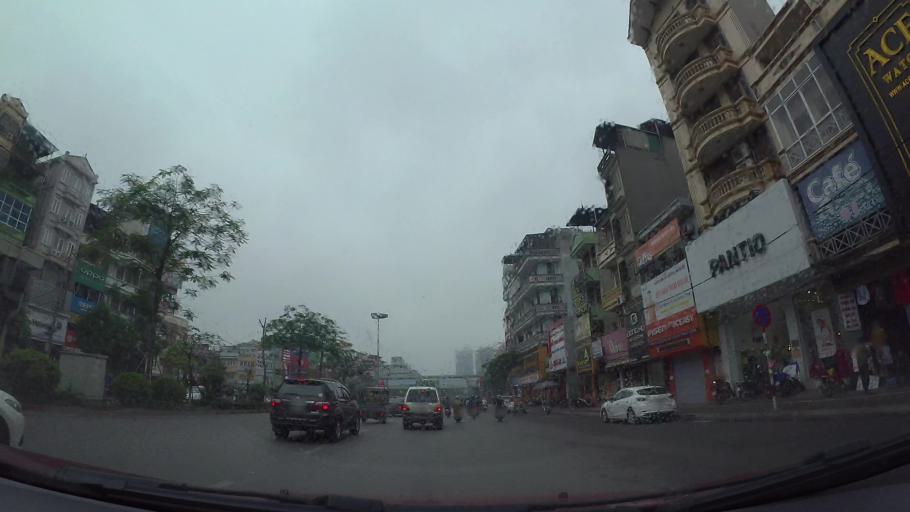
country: VN
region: Ha Noi
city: Dong Da
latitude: 21.0118
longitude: 105.8364
